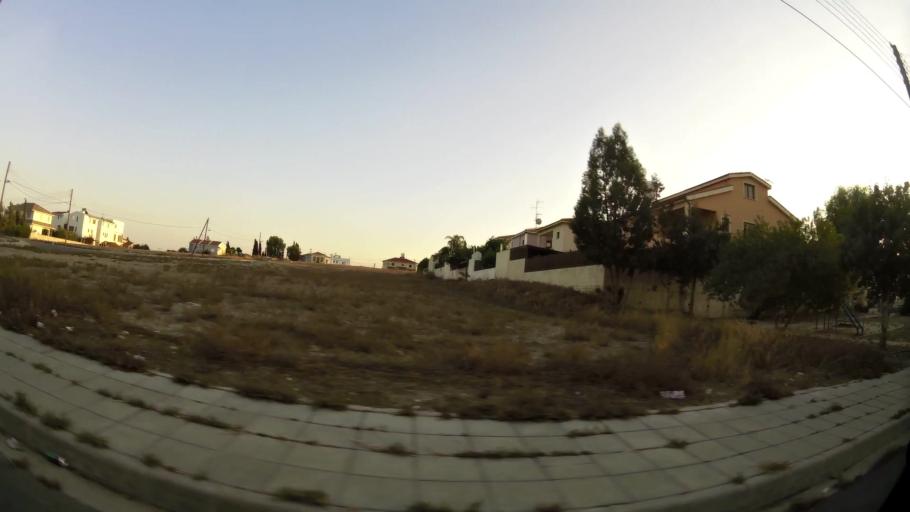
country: CY
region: Larnaka
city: Aradippou
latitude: 34.9145
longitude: 33.5860
